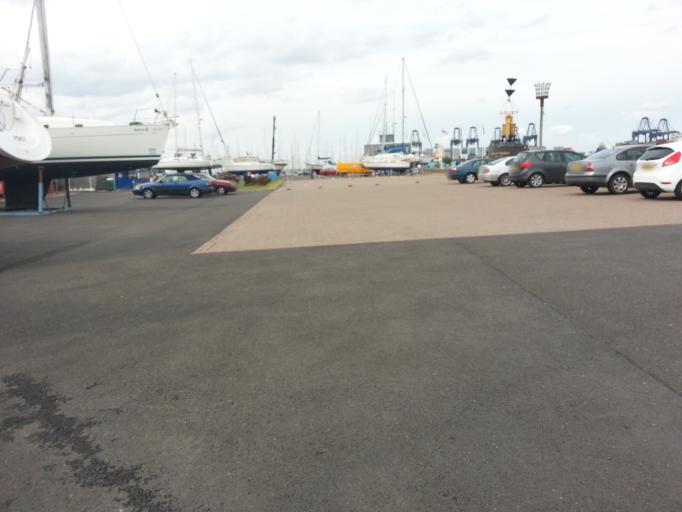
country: GB
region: England
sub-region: Suffolk
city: Shotley Gate
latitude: 51.9568
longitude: 1.2756
